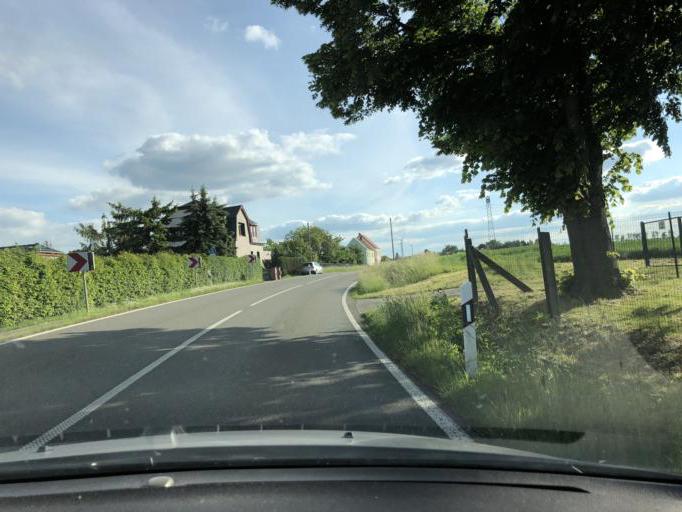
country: DE
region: Thuringia
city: Gossnitz
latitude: 50.8869
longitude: 12.4187
